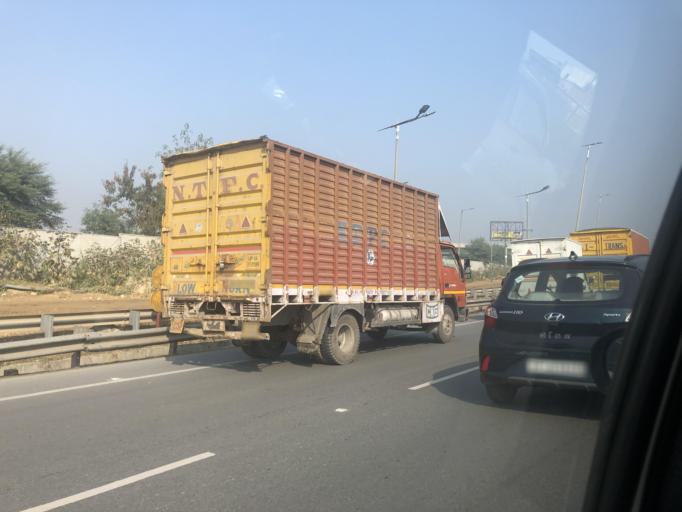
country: IN
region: Haryana
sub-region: Gurgaon
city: Gurgaon
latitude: 28.5382
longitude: 77.1159
